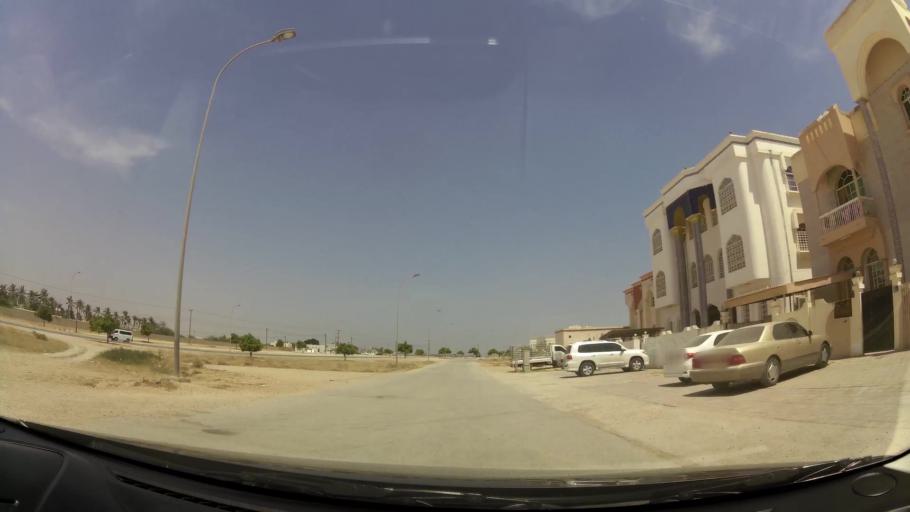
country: OM
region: Zufar
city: Salalah
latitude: 17.0586
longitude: 54.1627
